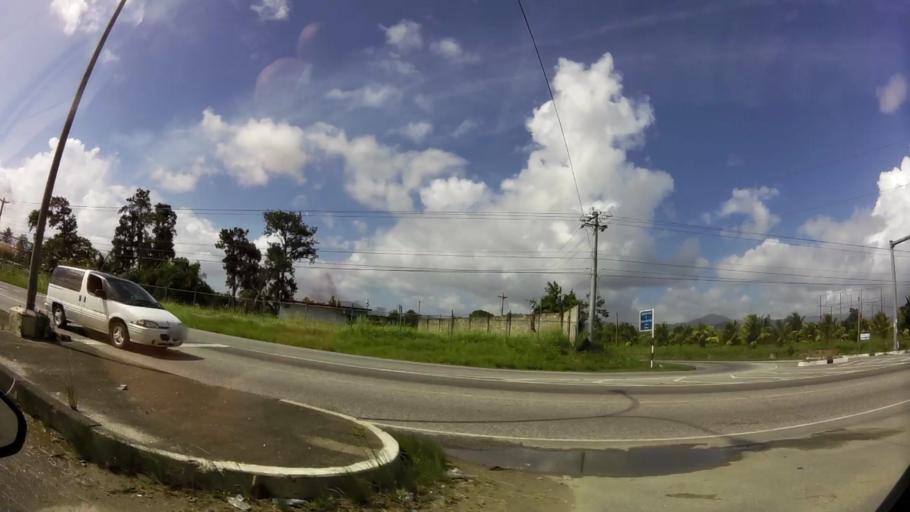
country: TT
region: Borough of Arima
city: Arima
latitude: 10.6199
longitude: -61.2539
